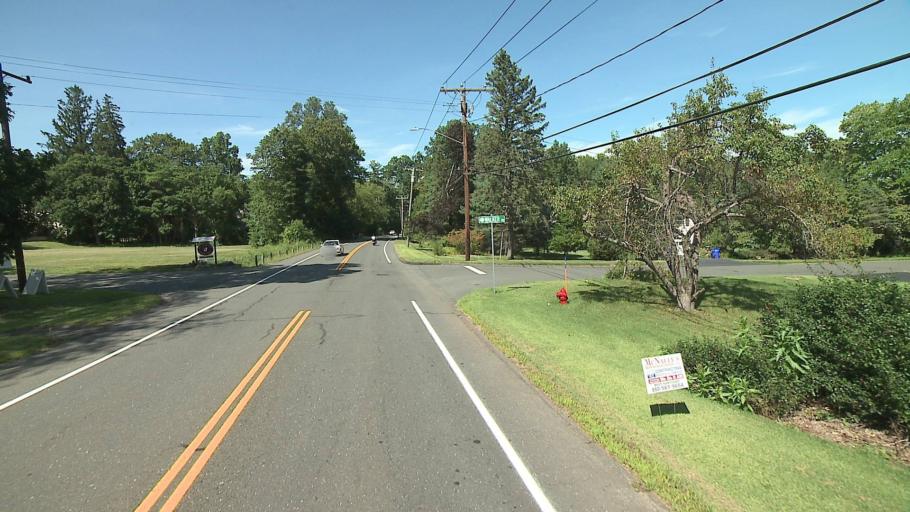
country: US
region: Connecticut
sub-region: Hartford County
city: Weatogue
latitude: 41.8532
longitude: -72.8340
